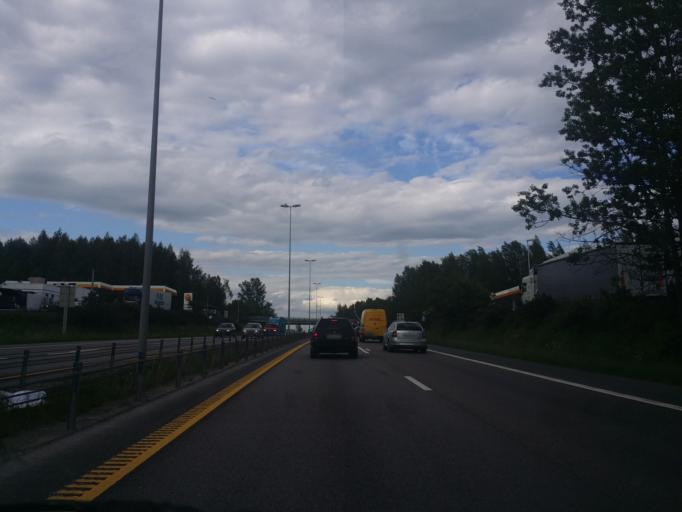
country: NO
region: Akershus
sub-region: Skedsmo
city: Lillestrom
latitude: 59.9969
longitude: 11.0383
